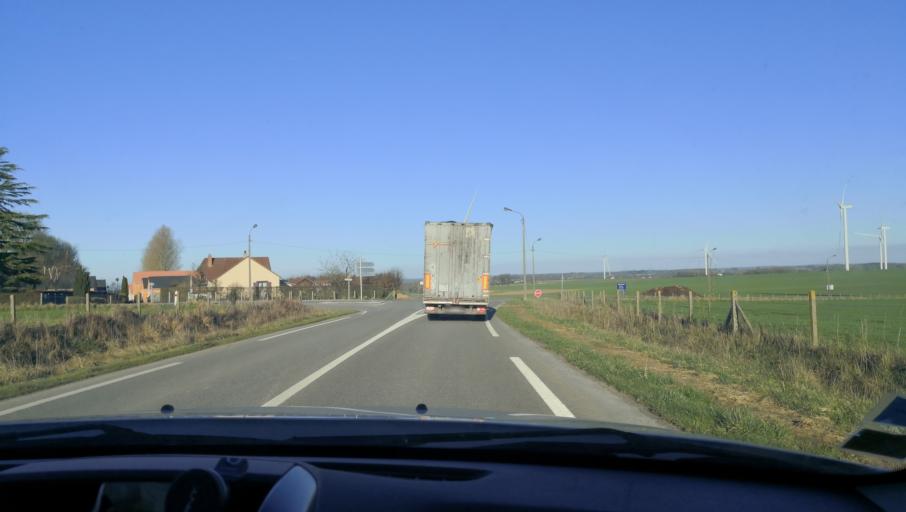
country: FR
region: Haute-Normandie
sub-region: Departement de la Seine-Maritime
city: Totes
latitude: 49.6763
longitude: 1.0527
